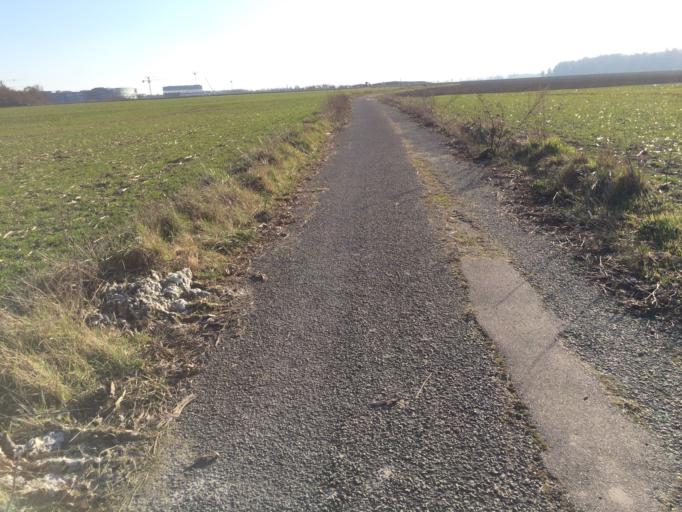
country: FR
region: Ile-de-France
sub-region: Departement de l'Essonne
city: Vauhallan
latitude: 48.7259
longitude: 2.1970
